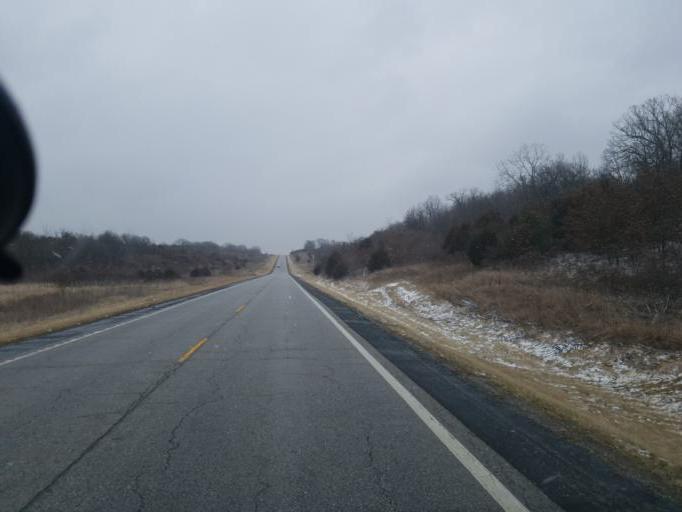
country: US
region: Missouri
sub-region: Putnam County
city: Unionville
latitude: 40.4653
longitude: -92.8513
